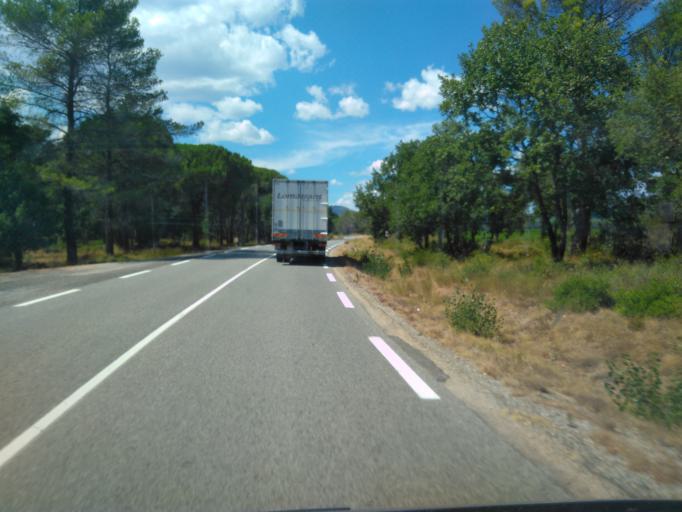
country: FR
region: Provence-Alpes-Cote d'Azur
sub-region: Departement du Var
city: Le Cannet-des-Maures
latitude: 43.3667
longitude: 6.3740
